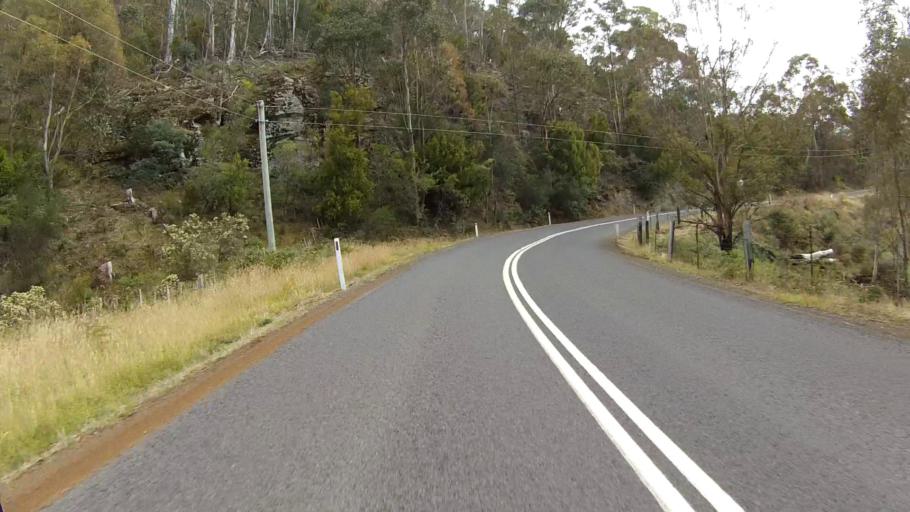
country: AU
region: Tasmania
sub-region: Clarence
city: Lindisfarne
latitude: -42.7834
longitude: 147.3581
